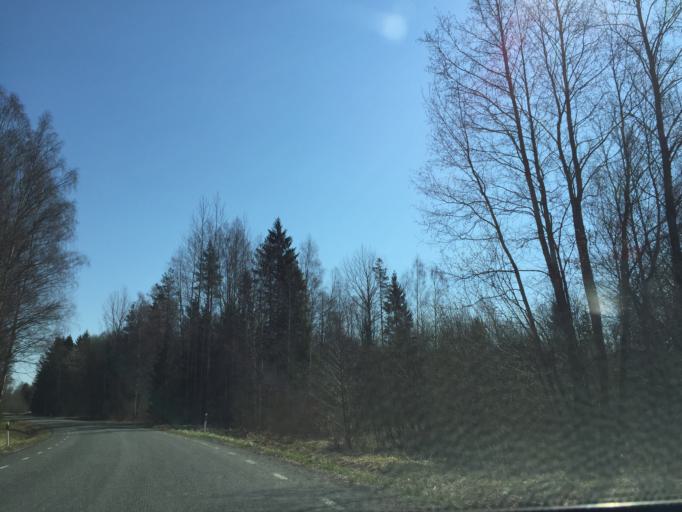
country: EE
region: Tartu
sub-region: Alatskivi vald
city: Kallaste
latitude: 58.5777
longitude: 26.9114
